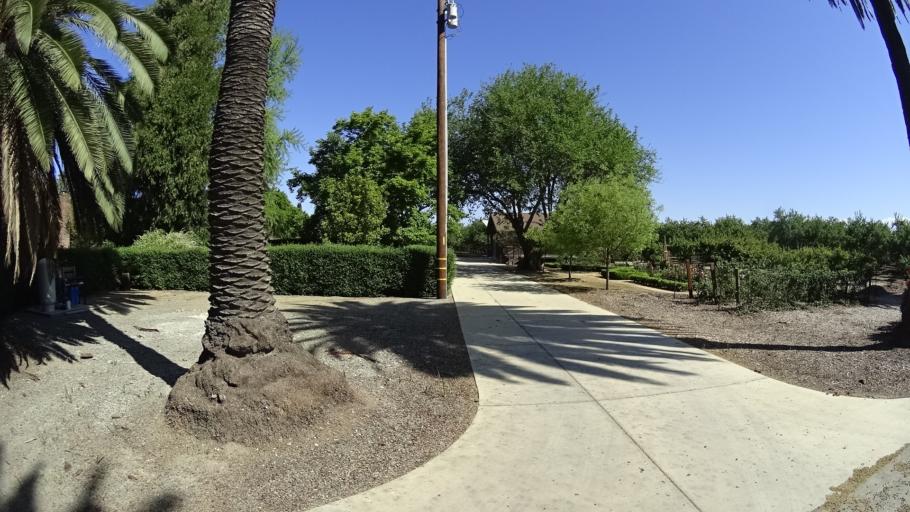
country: US
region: California
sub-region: Glenn County
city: Hamilton City
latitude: 39.7375
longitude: -122.0533
